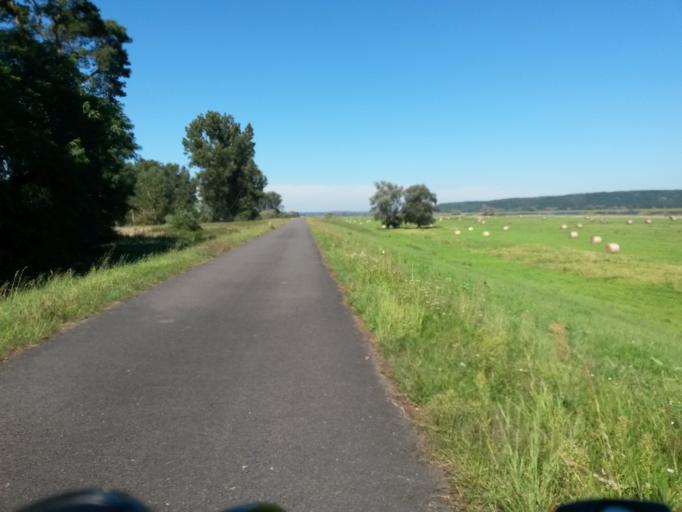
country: PL
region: West Pomeranian Voivodeship
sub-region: Powiat gryfinski
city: Cedynia
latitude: 52.9041
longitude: 14.1479
